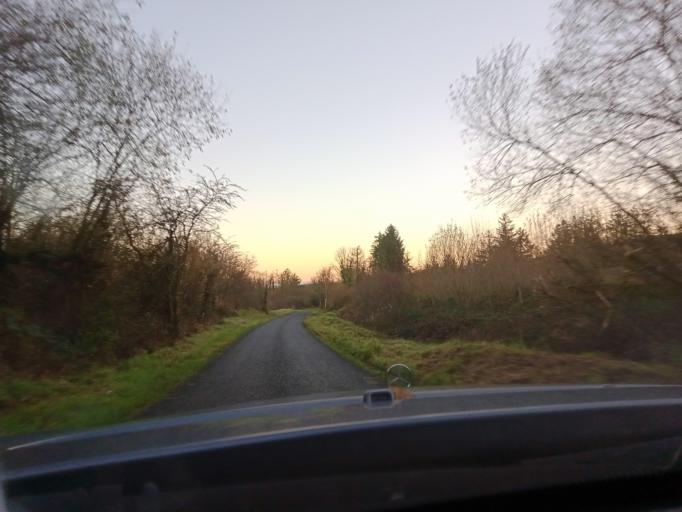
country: IE
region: Leinster
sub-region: Kilkenny
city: Thomastown
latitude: 52.4363
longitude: -7.1084
